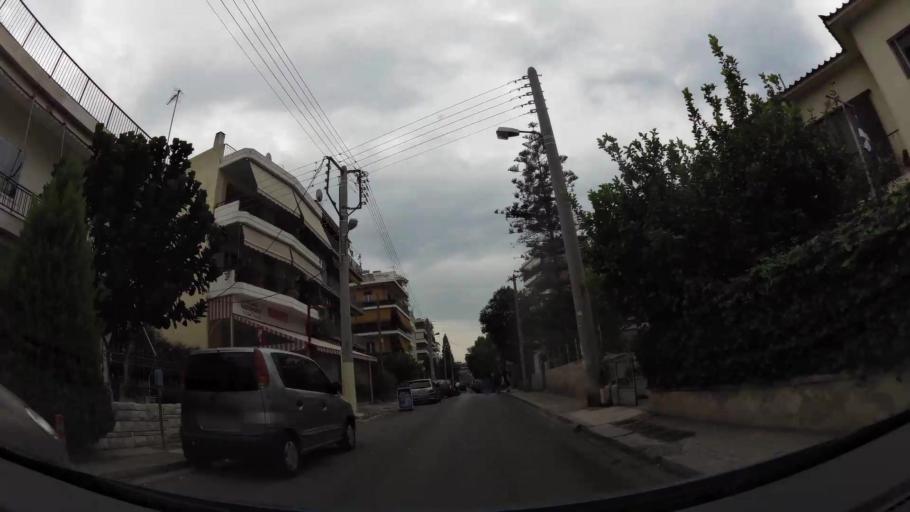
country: GR
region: Attica
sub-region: Nomarchia Athinas
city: Palaio Faliro
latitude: 37.9309
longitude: 23.7039
